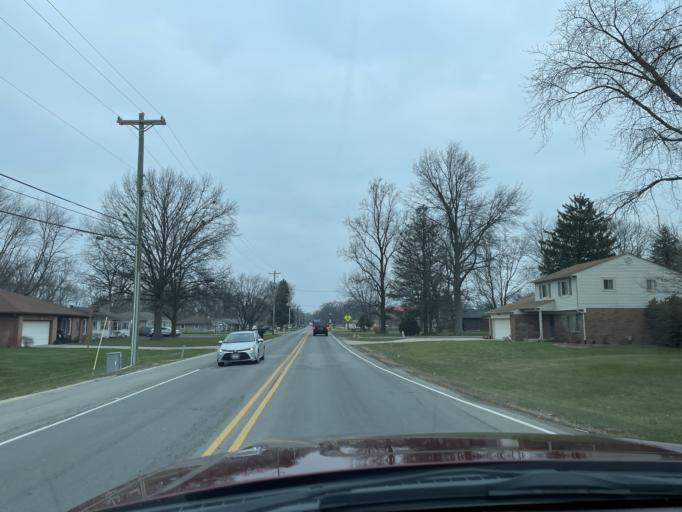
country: US
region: Indiana
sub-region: Hendricks County
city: Brownsburg
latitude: 39.8292
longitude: -86.4012
